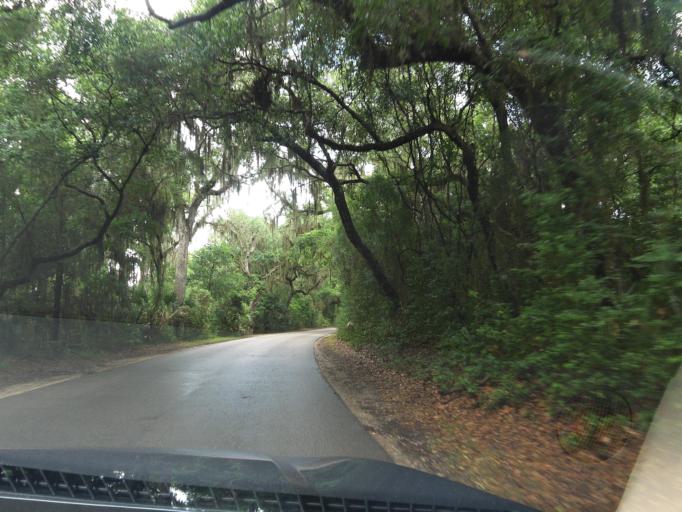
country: US
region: Florida
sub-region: Nassau County
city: Fernandina Beach
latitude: 30.6721
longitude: -81.4352
